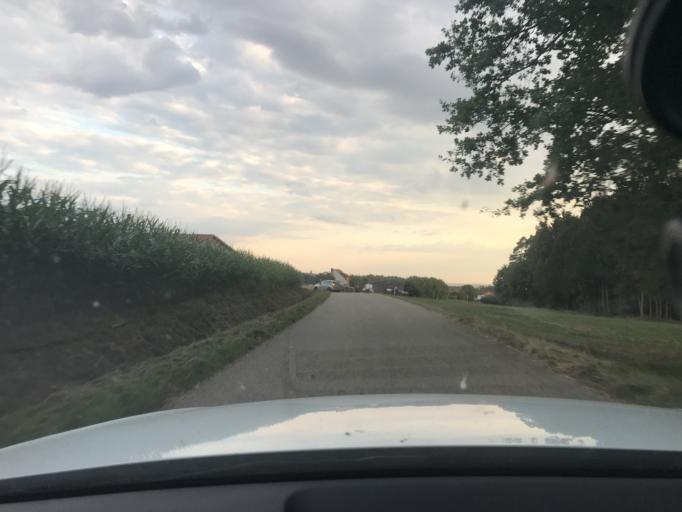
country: DE
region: Bavaria
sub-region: Upper Palatinate
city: Auerbach
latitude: 49.7398
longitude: 11.6141
